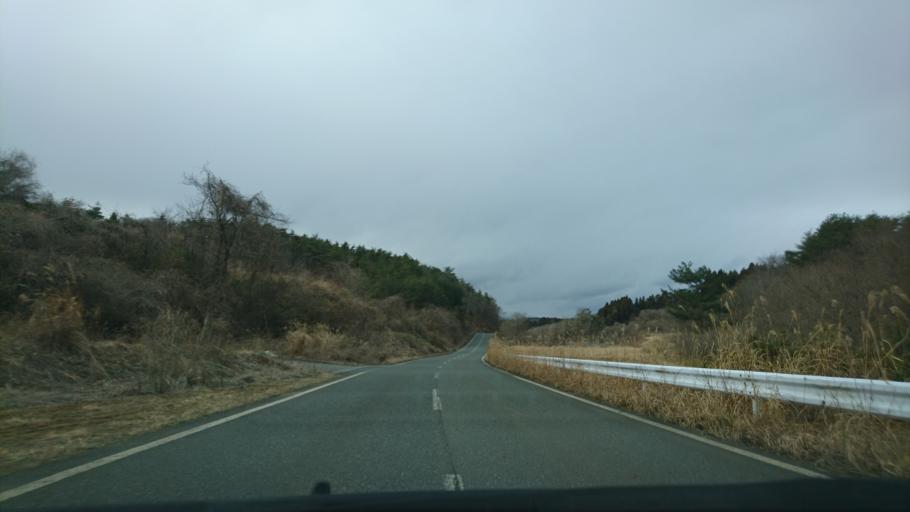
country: JP
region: Iwate
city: Ichinoseki
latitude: 38.8443
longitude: 141.2109
